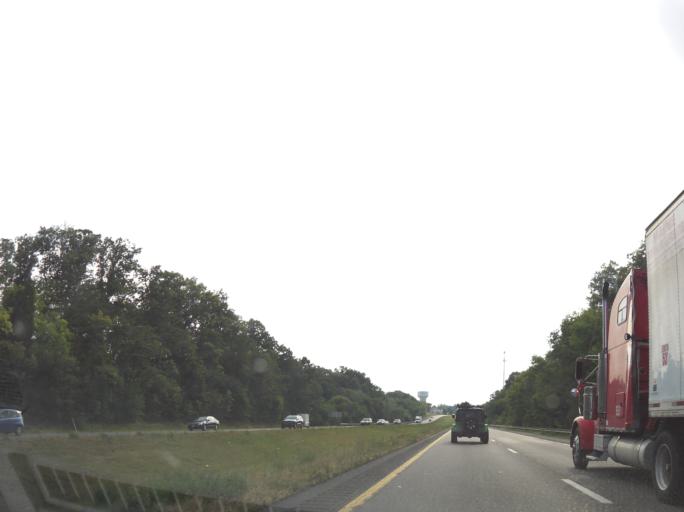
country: US
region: Maryland
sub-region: Washington County
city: Williamsport
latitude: 39.5826
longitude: -77.8599
